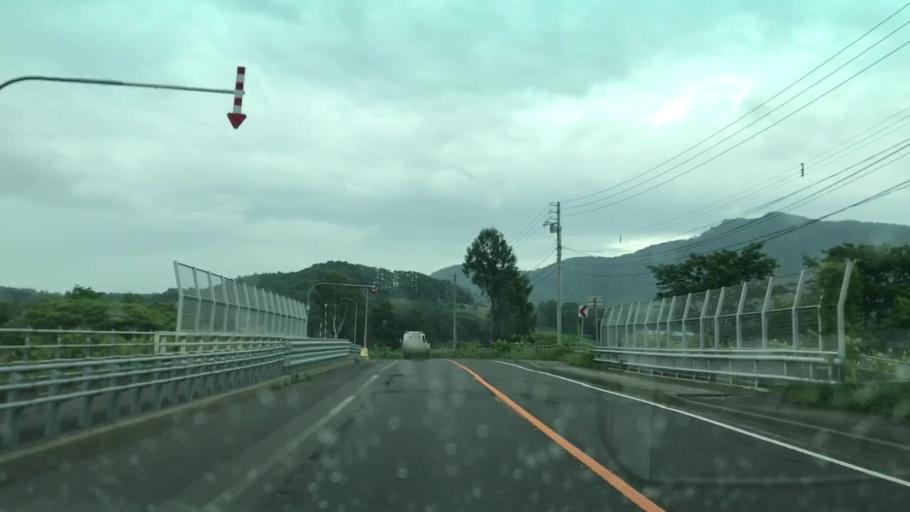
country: JP
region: Hokkaido
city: Niseko Town
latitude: 42.8099
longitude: 140.5379
